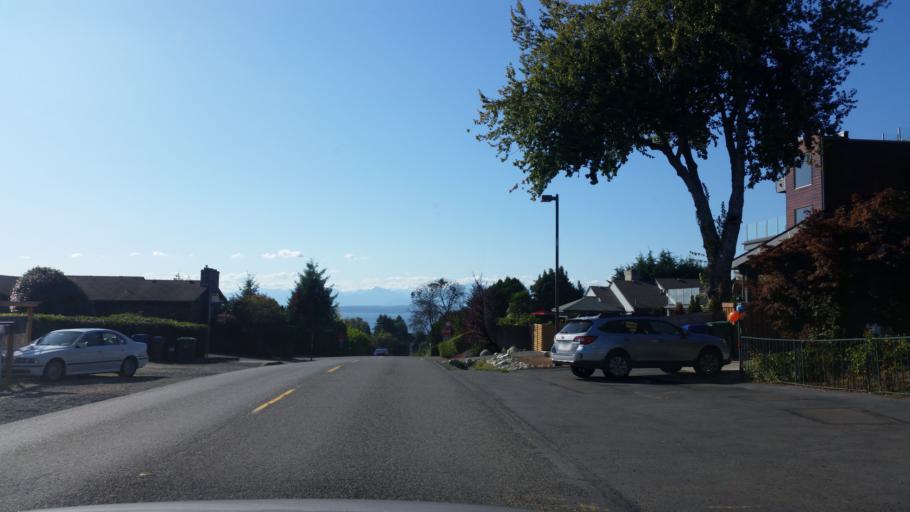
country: US
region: Washington
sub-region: King County
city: Shoreline
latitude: 47.7197
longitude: -122.3654
